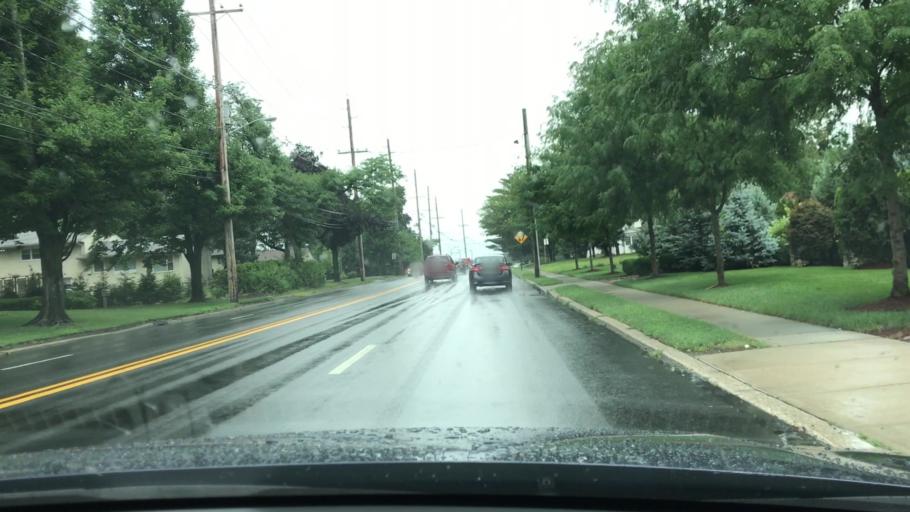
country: US
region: New Jersey
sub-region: Bergen County
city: Paramus
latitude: 40.9621
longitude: -74.0612
